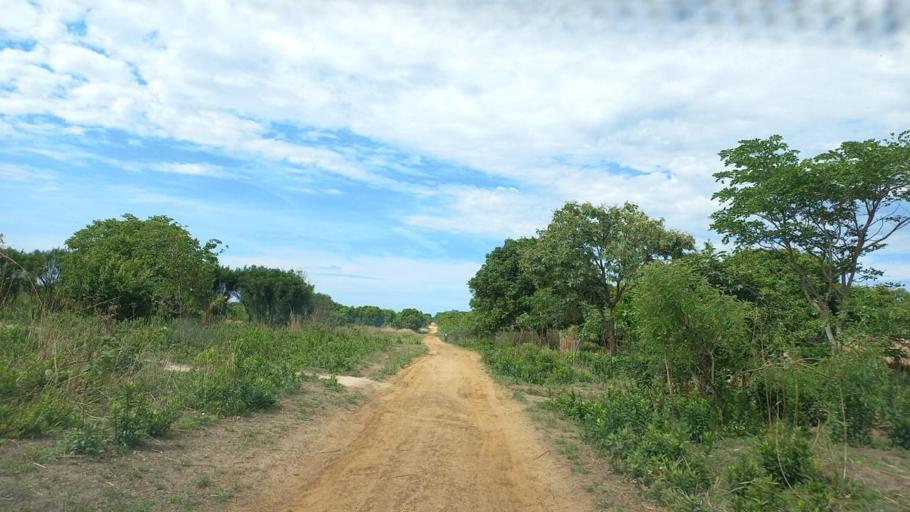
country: ZM
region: North-Western
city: Kabompo
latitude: -13.5148
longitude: 24.3900
